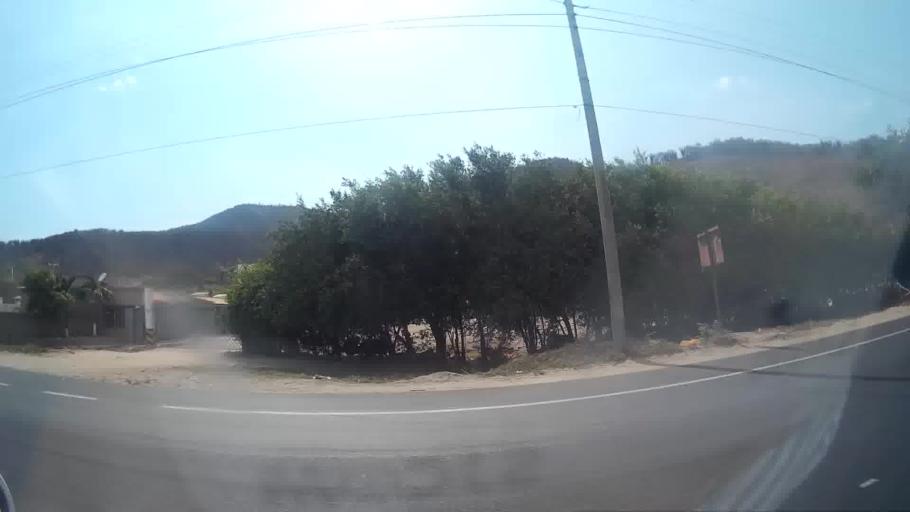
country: CO
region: Magdalena
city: Santa Marta
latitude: 11.1970
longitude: -74.2033
